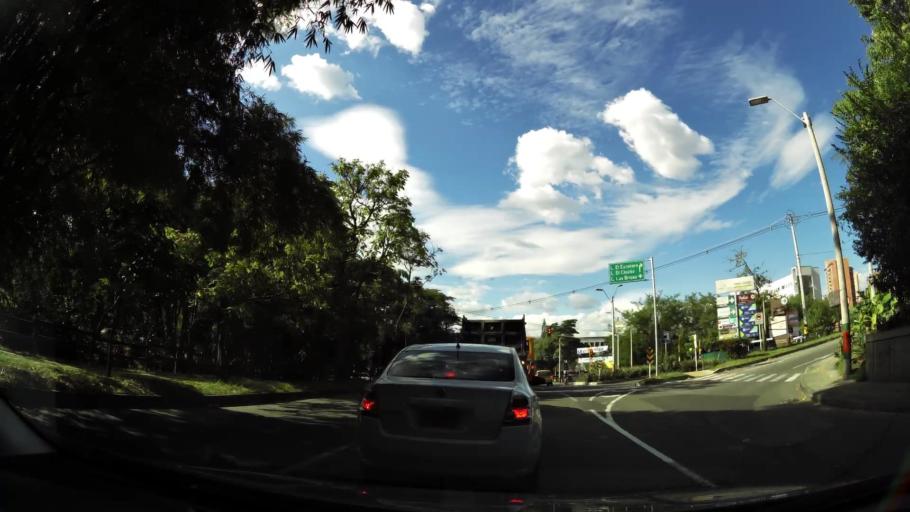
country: CO
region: Antioquia
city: Envigado
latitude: 6.1654
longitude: -75.5801
